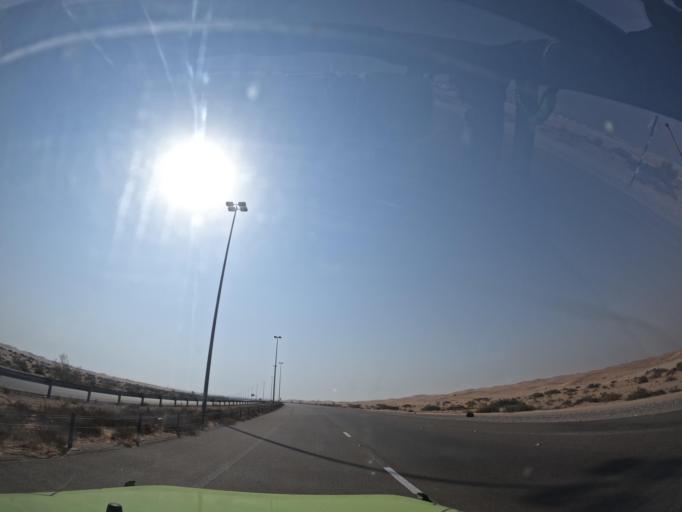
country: OM
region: Al Buraimi
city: Al Buraymi
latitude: 24.5193
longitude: 55.5553
